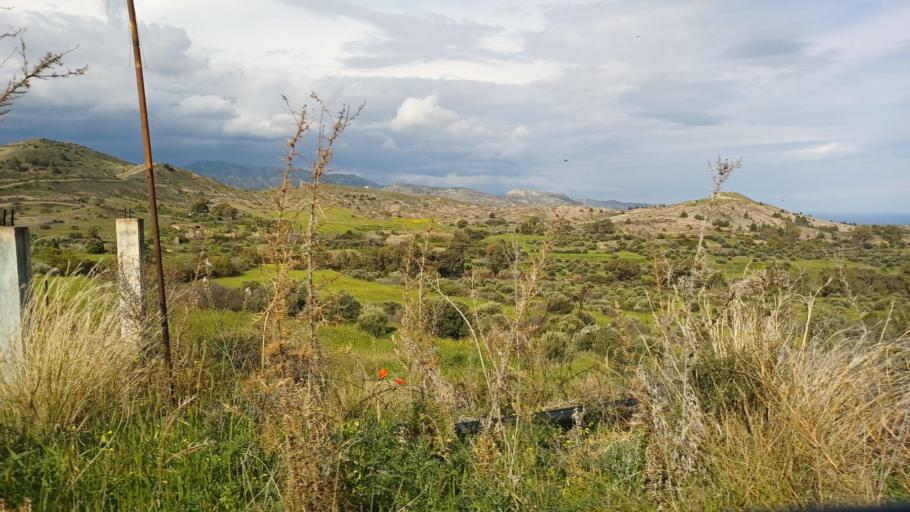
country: CY
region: Lefkosia
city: Lefka
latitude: 35.1036
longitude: 32.8869
